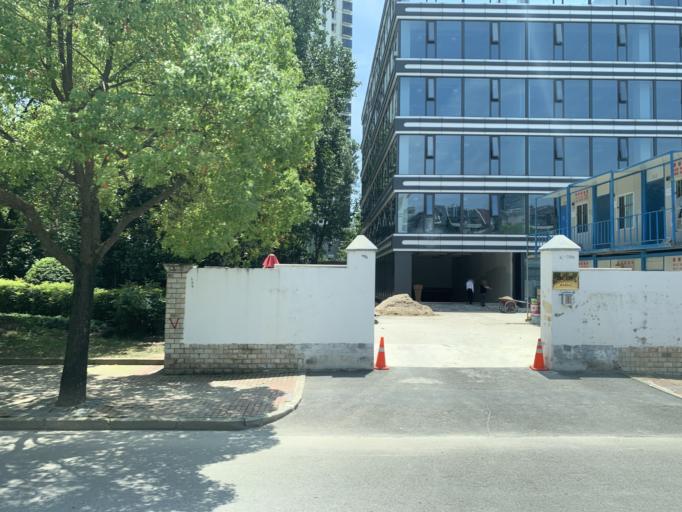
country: CN
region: Shanghai Shi
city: Pudong
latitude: 31.2389
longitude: 121.5296
